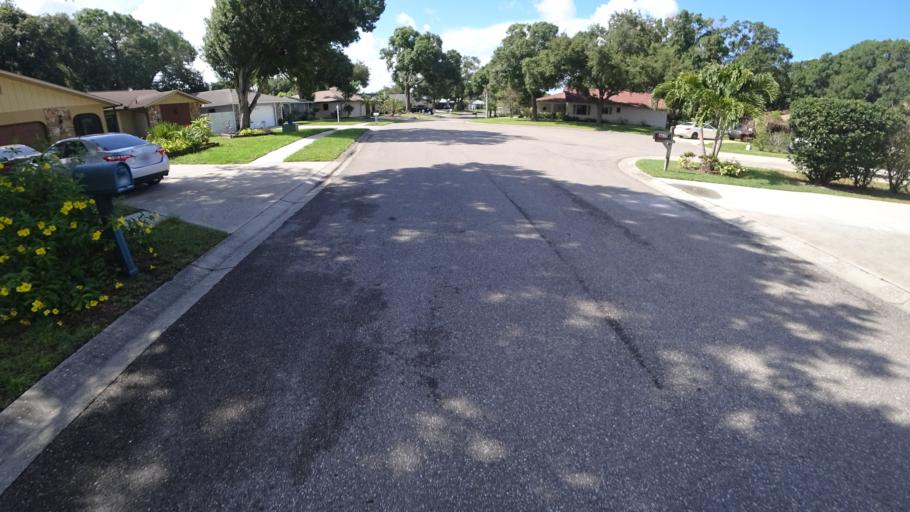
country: US
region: Florida
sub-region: Sarasota County
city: Desoto Lakes
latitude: 27.3915
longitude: -82.4994
